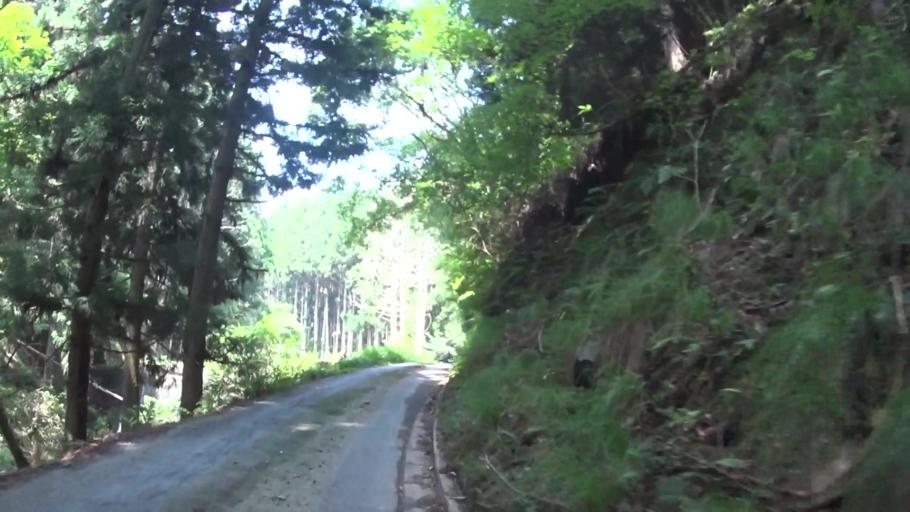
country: JP
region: Kyoto
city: Ayabe
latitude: 35.3016
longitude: 135.3980
